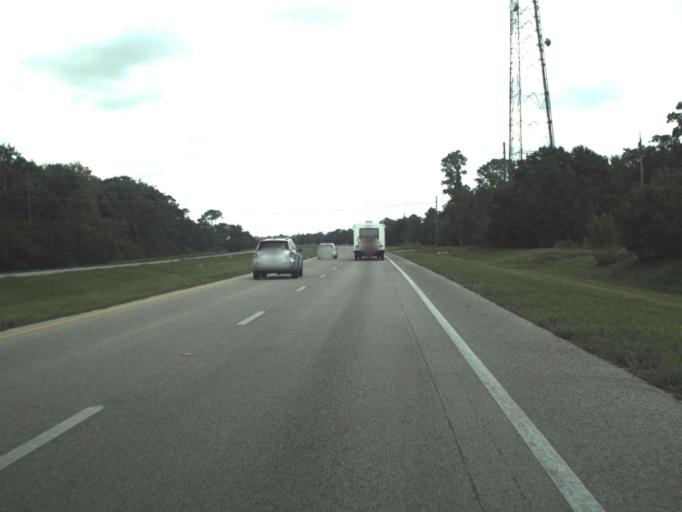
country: US
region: Florida
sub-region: Indian River County
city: Fellsmere
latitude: 27.6706
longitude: -80.8041
